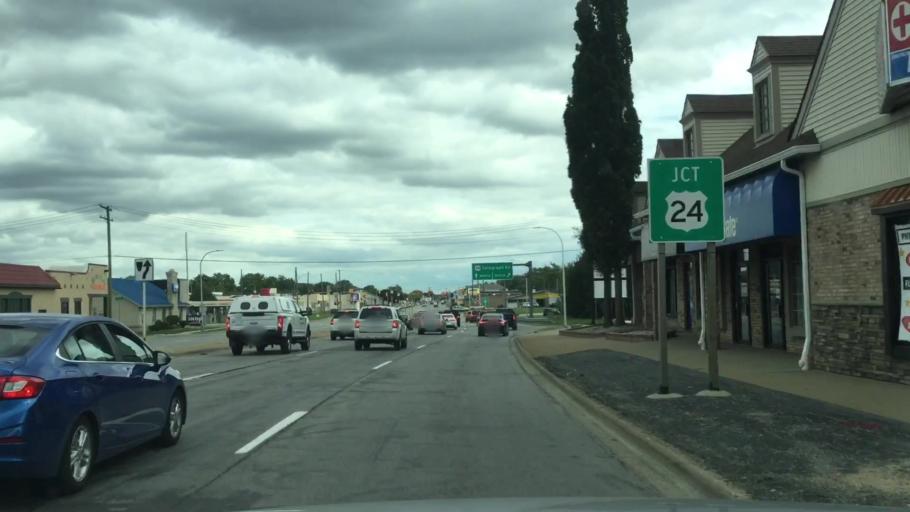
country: US
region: Michigan
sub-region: Wayne County
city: Dearborn Heights
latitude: 42.3269
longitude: -83.2759
